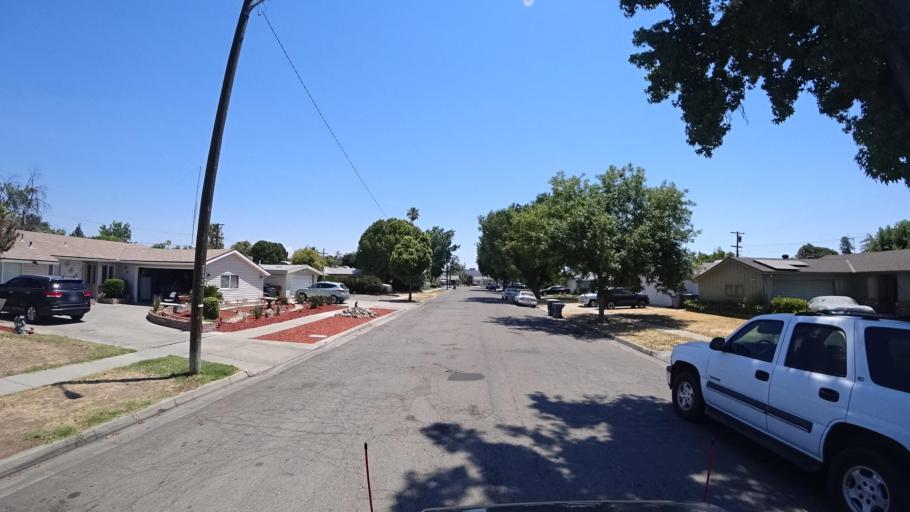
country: US
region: California
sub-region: Fresno County
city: Fresno
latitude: 36.7950
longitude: -119.7602
